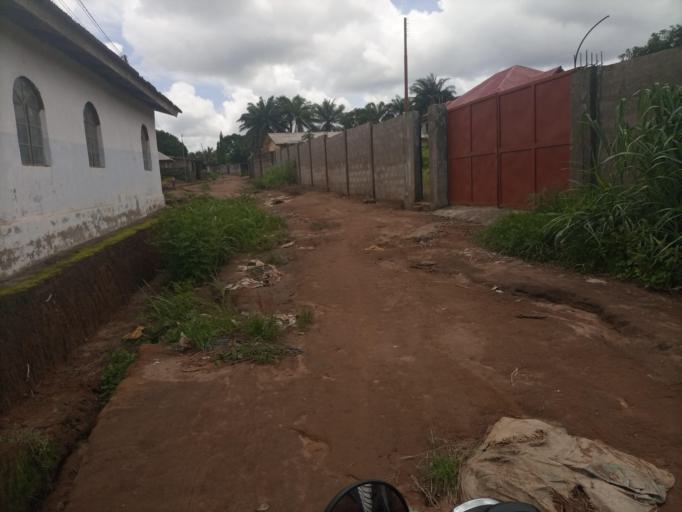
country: SL
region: Northern Province
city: Masoyila
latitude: 8.5927
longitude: -13.1675
